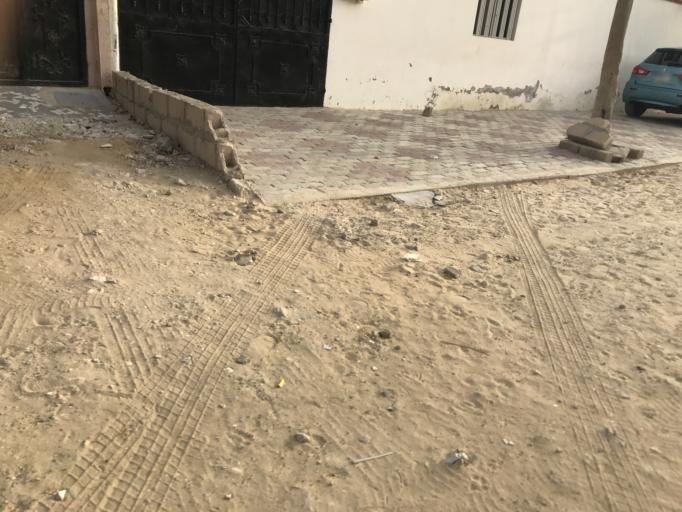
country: SN
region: Saint-Louis
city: Saint-Louis
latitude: 16.0372
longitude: -16.4459
